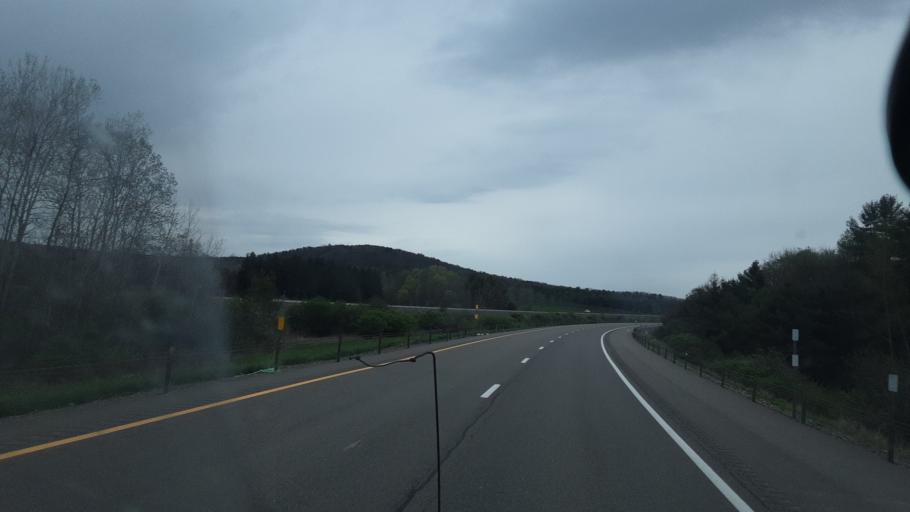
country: US
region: New York
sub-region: Allegany County
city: Belmont
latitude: 42.3006
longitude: -77.9509
